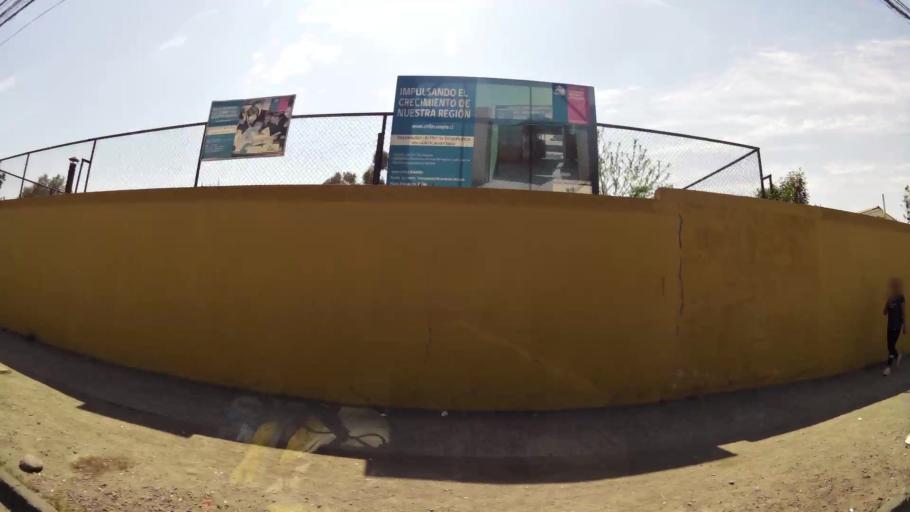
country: CL
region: Santiago Metropolitan
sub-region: Provincia de Santiago
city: La Pintana
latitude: -33.5460
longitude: -70.6445
